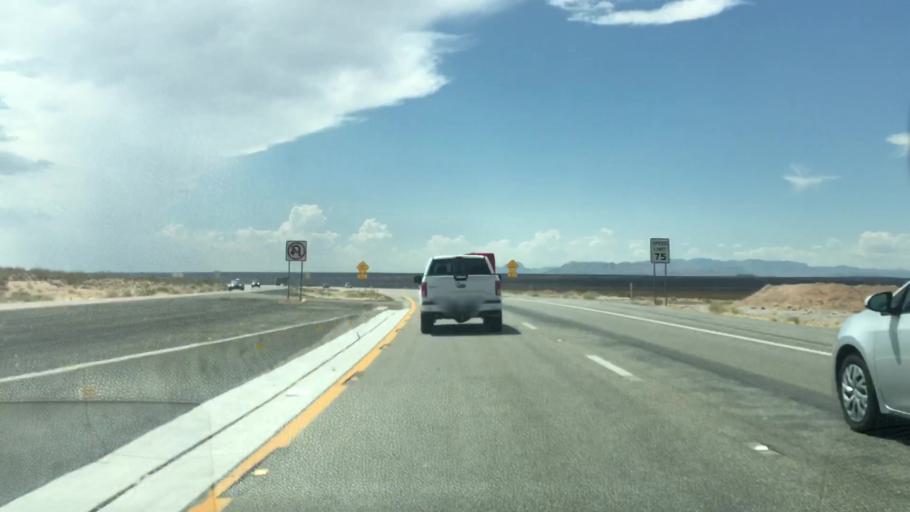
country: US
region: Arizona
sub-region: Mohave County
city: Beaver Dam
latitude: 36.9180
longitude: -113.8714
